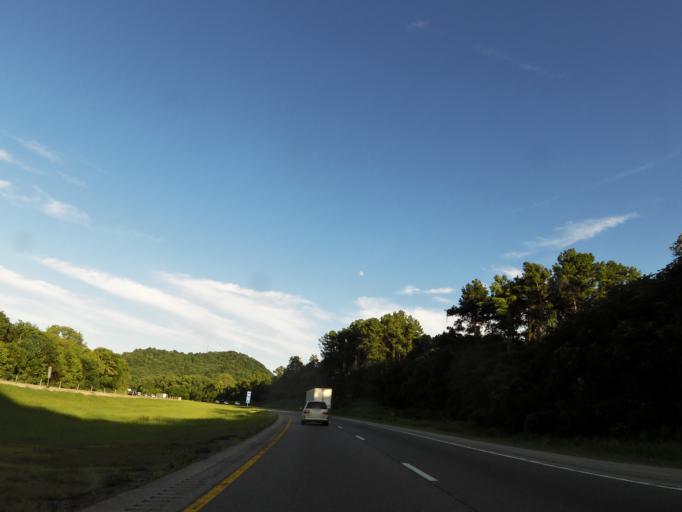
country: US
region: Tennessee
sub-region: Smith County
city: Gordonsville
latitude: 36.1476
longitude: -85.8700
